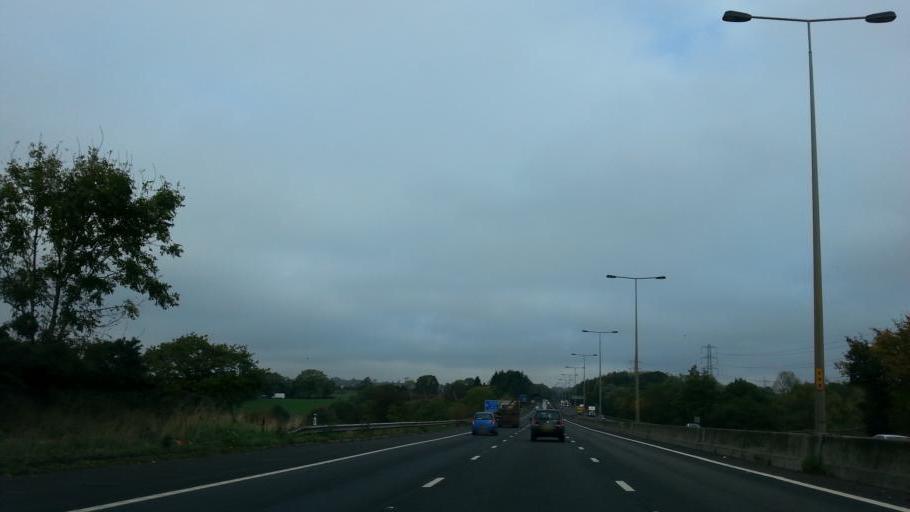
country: GB
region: England
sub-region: City and Borough of Birmingham
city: Bartley Green
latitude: 52.4351
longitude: -2.0176
